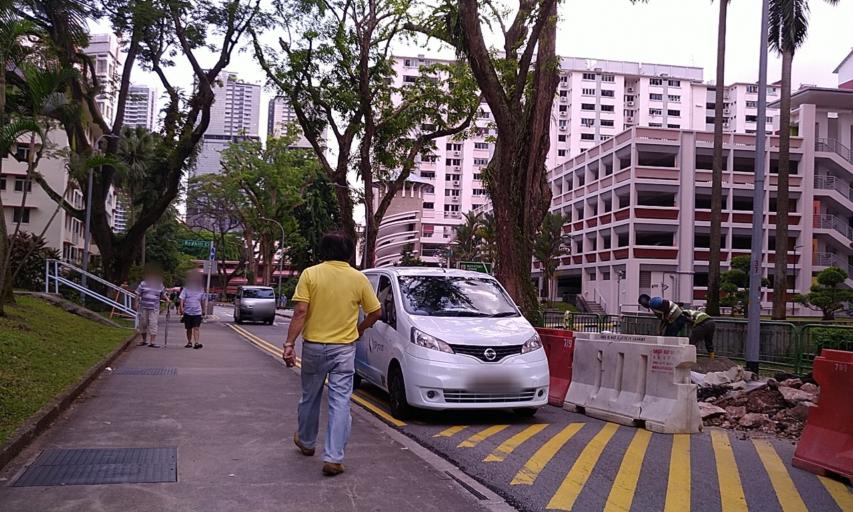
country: SG
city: Singapore
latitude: 1.2858
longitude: 103.8182
